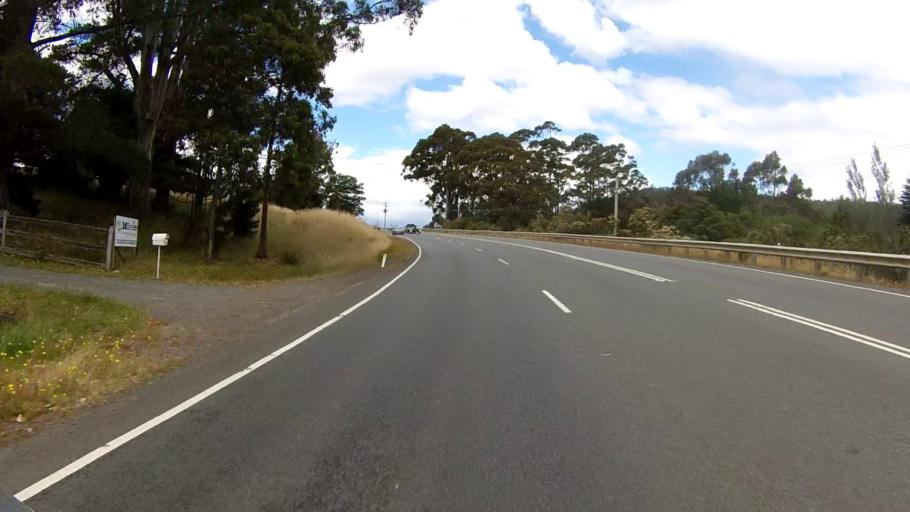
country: AU
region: Tasmania
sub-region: Huon Valley
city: Huonville
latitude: -42.9768
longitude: 147.1516
